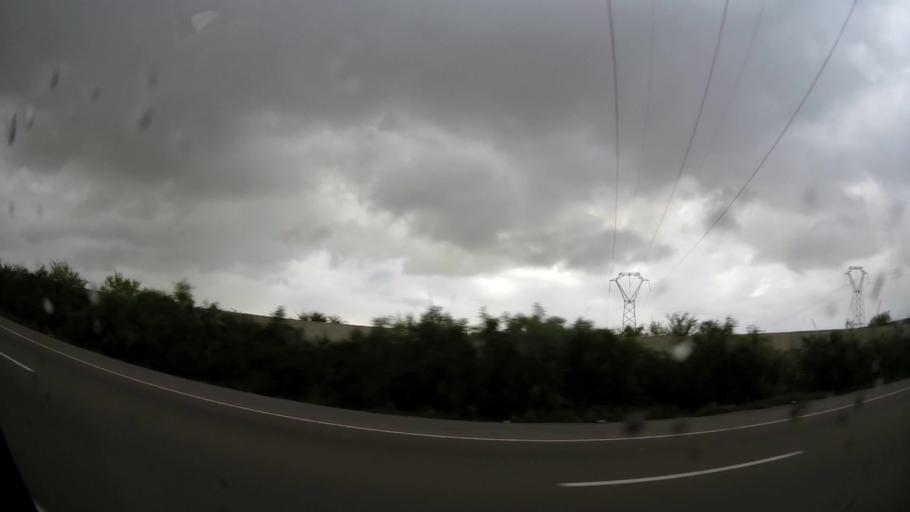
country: MA
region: Grand Casablanca
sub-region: Mohammedia
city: Mohammedia
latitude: 33.6535
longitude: -7.4141
